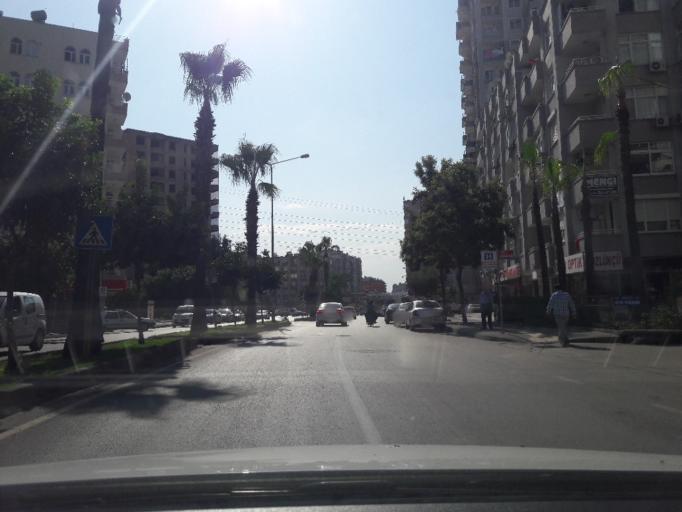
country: TR
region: Adana
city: Adana
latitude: 37.0174
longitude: 35.3216
